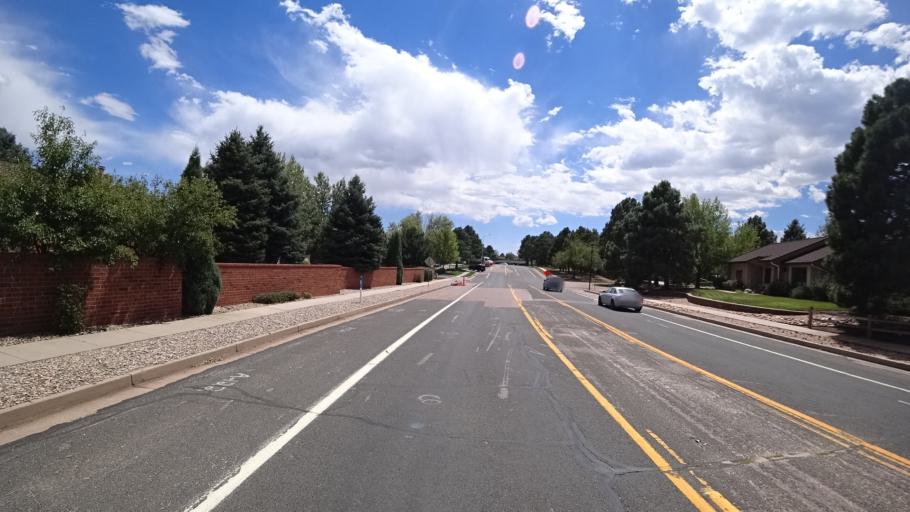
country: US
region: Colorado
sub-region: El Paso County
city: Colorado Springs
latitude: 38.7909
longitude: -104.8255
